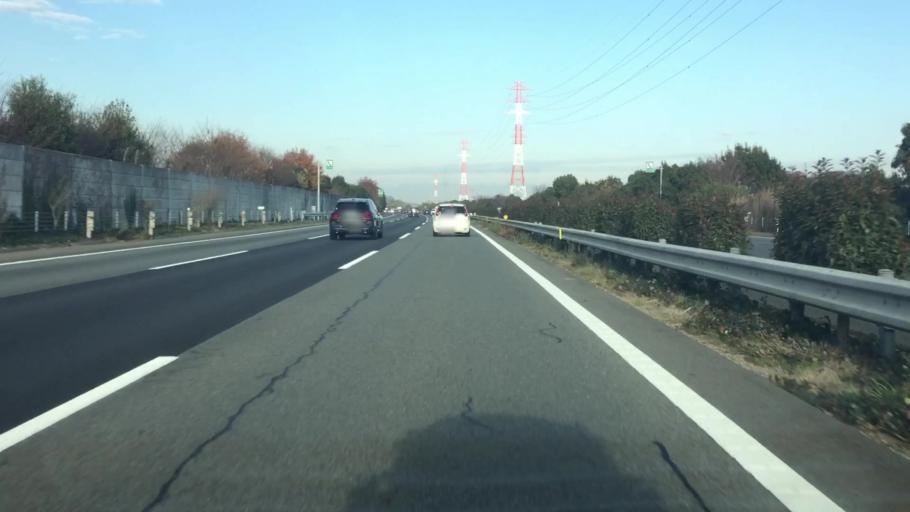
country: JP
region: Saitama
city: Yorii
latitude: 36.1572
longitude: 139.2141
